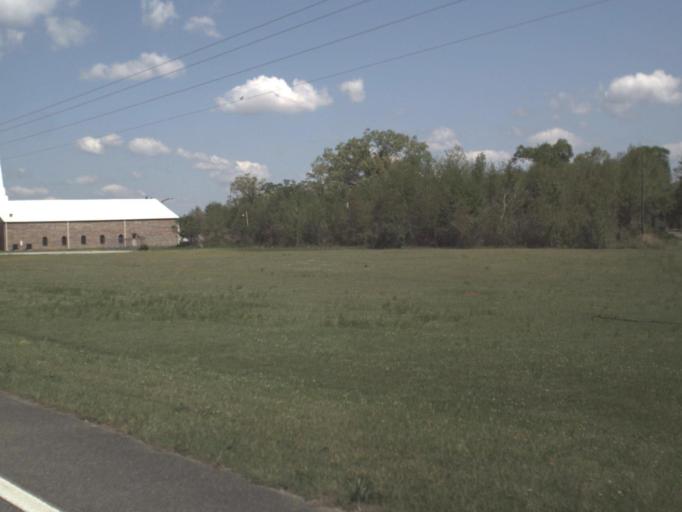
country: US
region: Alabama
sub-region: Escambia County
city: East Brewton
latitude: 30.9031
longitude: -87.0317
